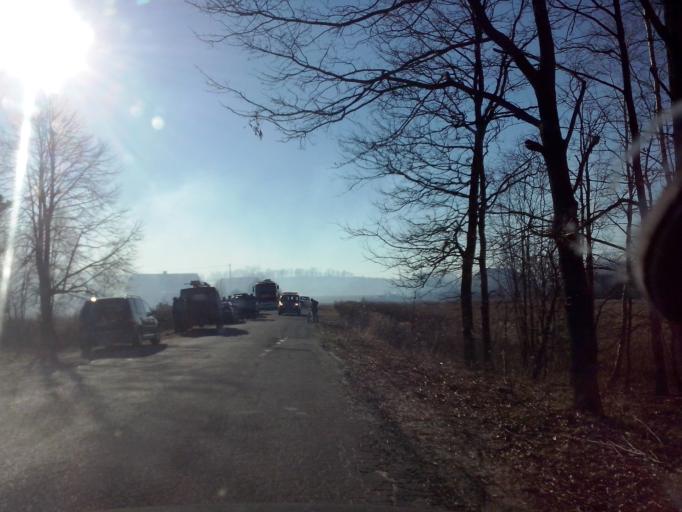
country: PL
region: Subcarpathian Voivodeship
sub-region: Powiat nizanski
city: Harasiuki
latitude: 50.4726
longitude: 22.5257
